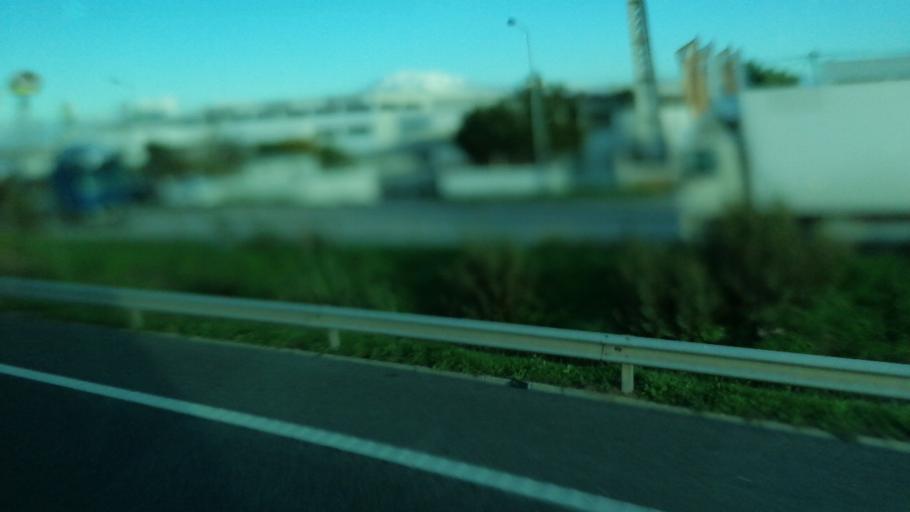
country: PT
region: Lisbon
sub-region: Vila Franca de Xira
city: Castanheira do Ribatejo
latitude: 38.9746
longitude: -8.9777
